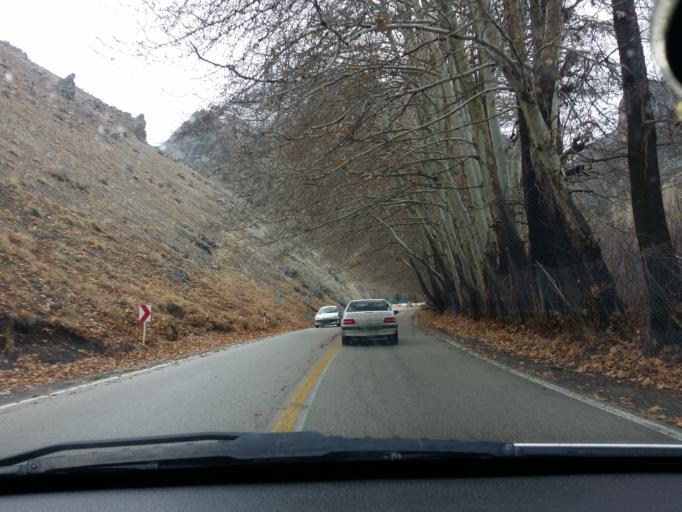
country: IR
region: Tehran
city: Tajrish
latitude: 36.0264
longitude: 51.2468
